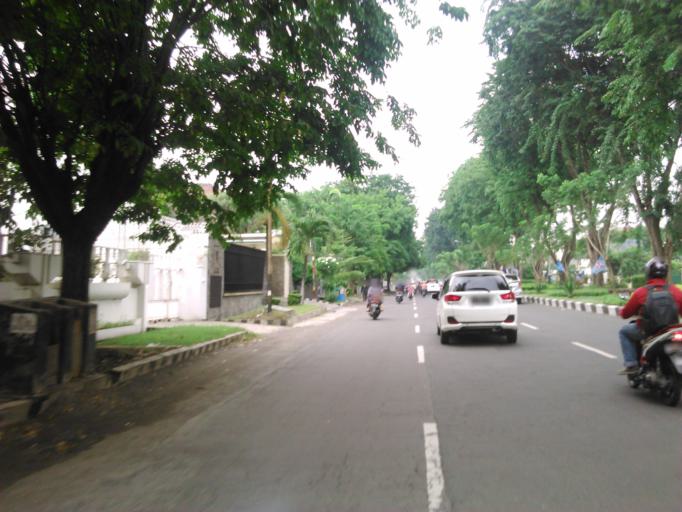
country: ID
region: East Java
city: Mulyorejo
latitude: -7.2807
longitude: 112.7778
